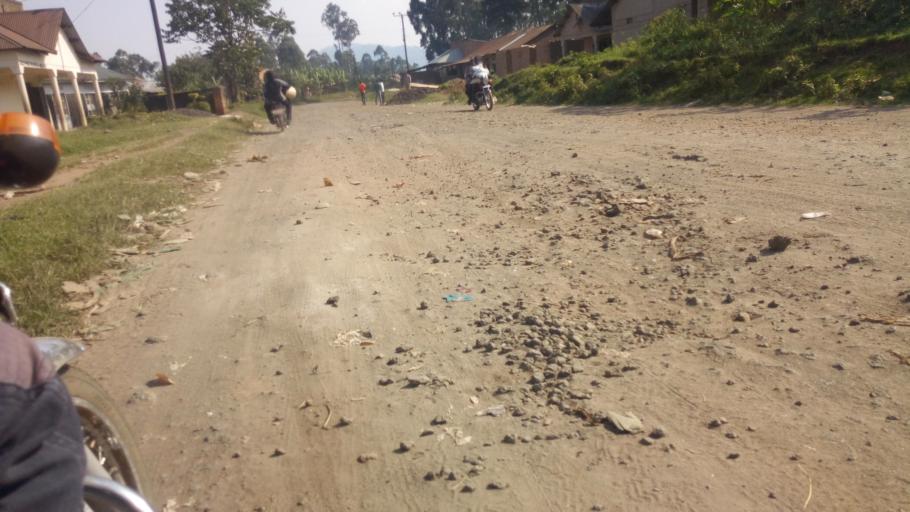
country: UG
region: Western Region
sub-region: Kisoro District
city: Kisoro
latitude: -1.2500
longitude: 29.7134
